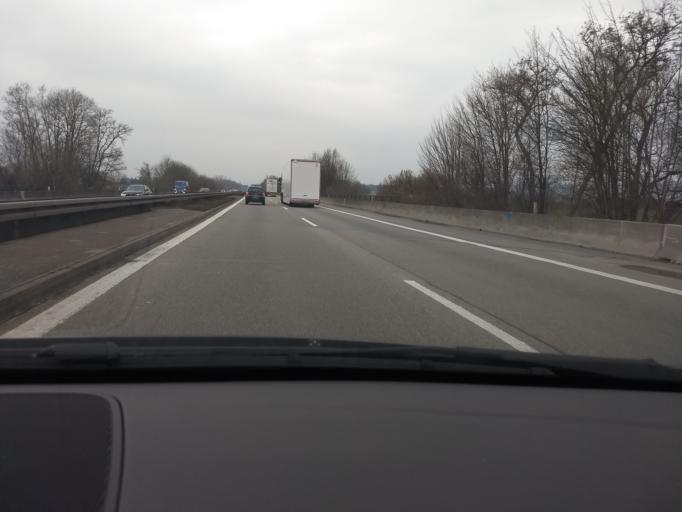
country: DE
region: Baden-Wuerttemberg
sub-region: Freiburg Region
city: Riegel
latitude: 48.1422
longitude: 7.7709
